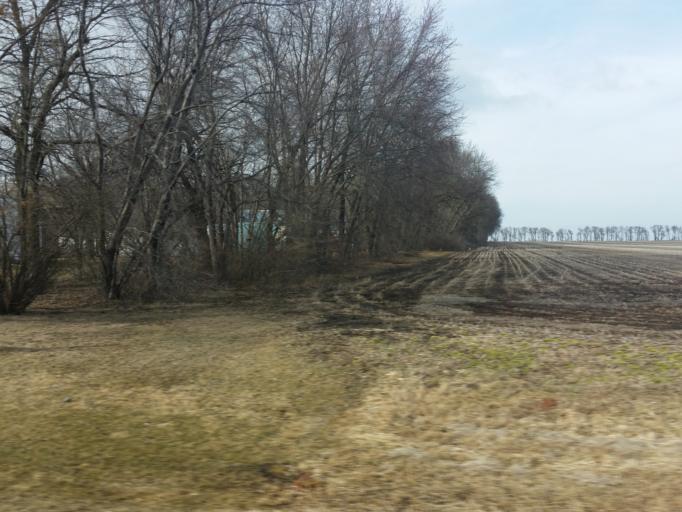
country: US
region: North Dakota
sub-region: Richland County
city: Wahpeton
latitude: 46.4712
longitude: -96.6664
